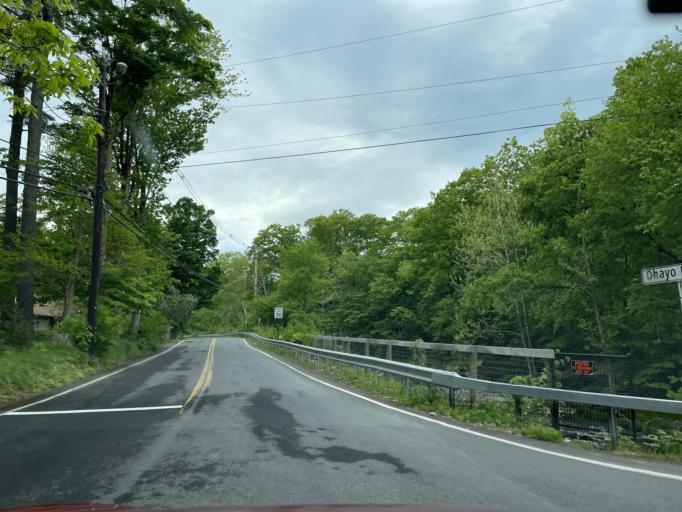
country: US
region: New York
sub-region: Ulster County
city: Woodstock
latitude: 42.0370
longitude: -74.1188
